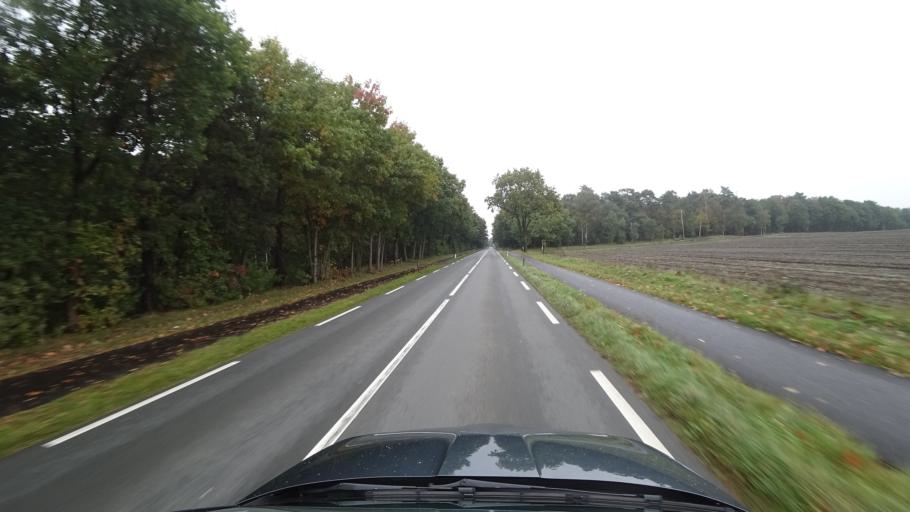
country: NL
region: Gelderland
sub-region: Gemeente Renkum
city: Wolfheze
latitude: 52.0133
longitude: 5.8006
